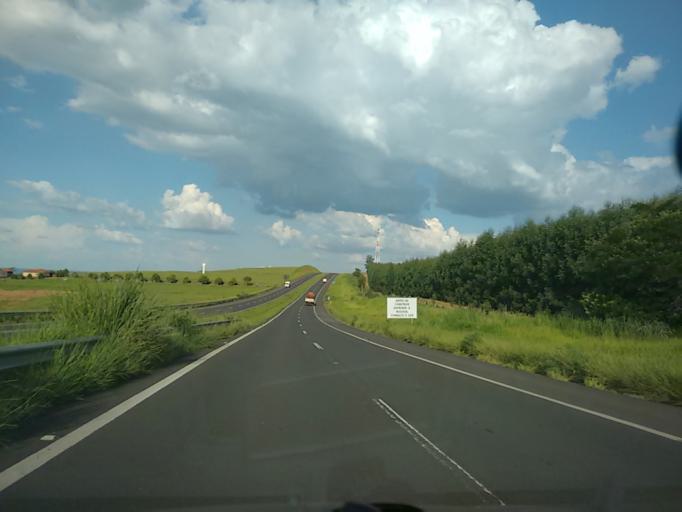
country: BR
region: Sao Paulo
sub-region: Duartina
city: Duartina
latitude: -22.3251
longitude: -49.4254
